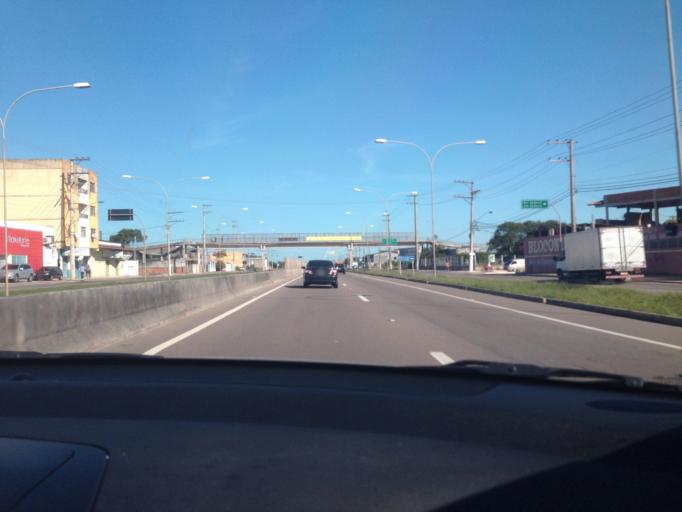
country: BR
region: Espirito Santo
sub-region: Vila Velha
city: Vila Velha
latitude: -20.4300
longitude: -40.3307
